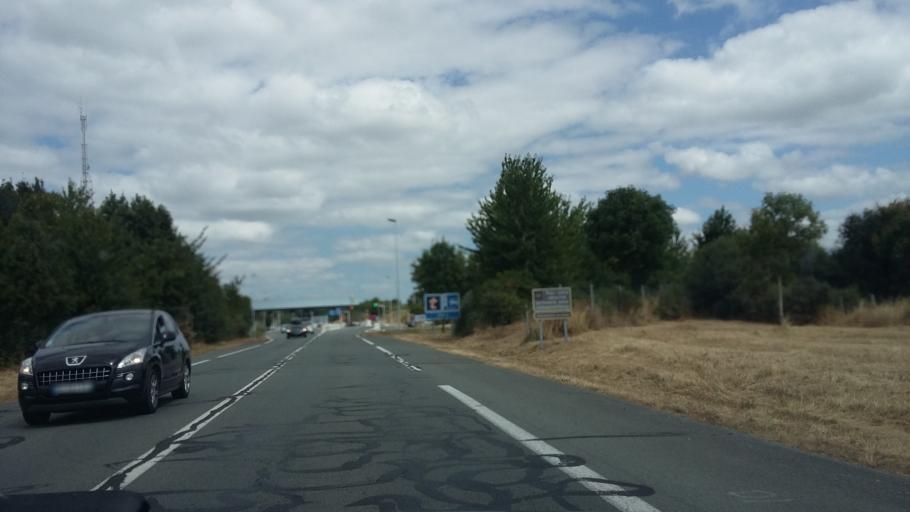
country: FR
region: Pays de la Loire
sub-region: Departement de la Vendee
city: Bournezeau
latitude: 46.6269
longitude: -1.1577
